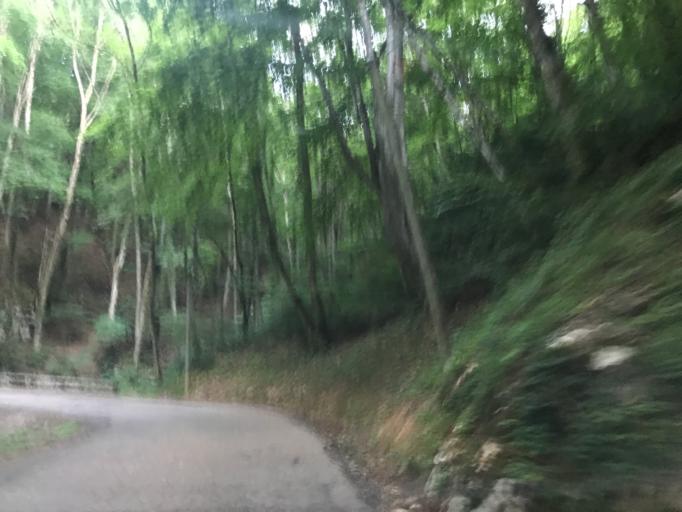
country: FR
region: Rhone-Alpes
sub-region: Departement de l'Isere
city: Saint-Vincent-de-Mercuze
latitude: 45.3881
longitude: 5.9328
